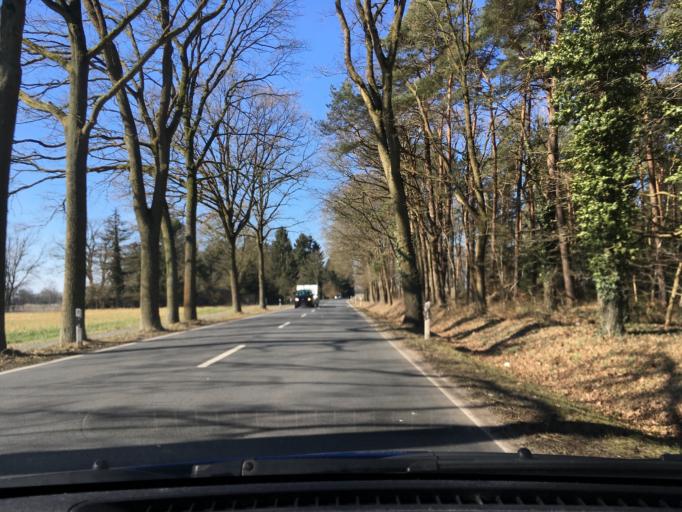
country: DE
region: Lower Saxony
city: Brockel
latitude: 53.0915
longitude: 9.5430
